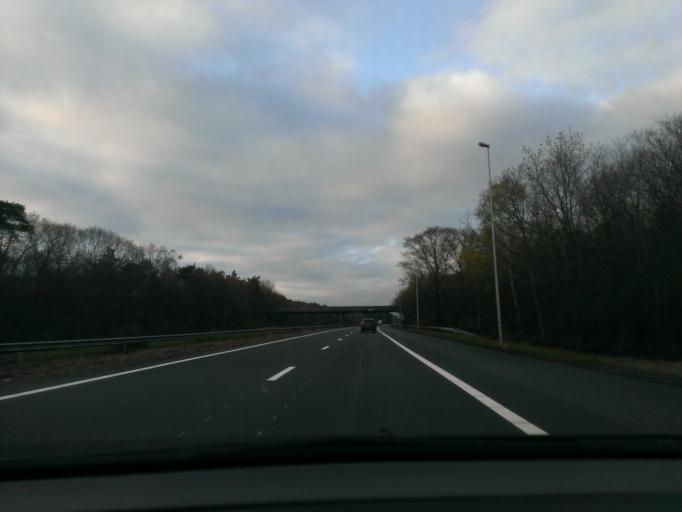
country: NL
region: Gelderland
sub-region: Gemeente Hattem
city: Hattem
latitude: 52.4433
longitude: 6.0229
